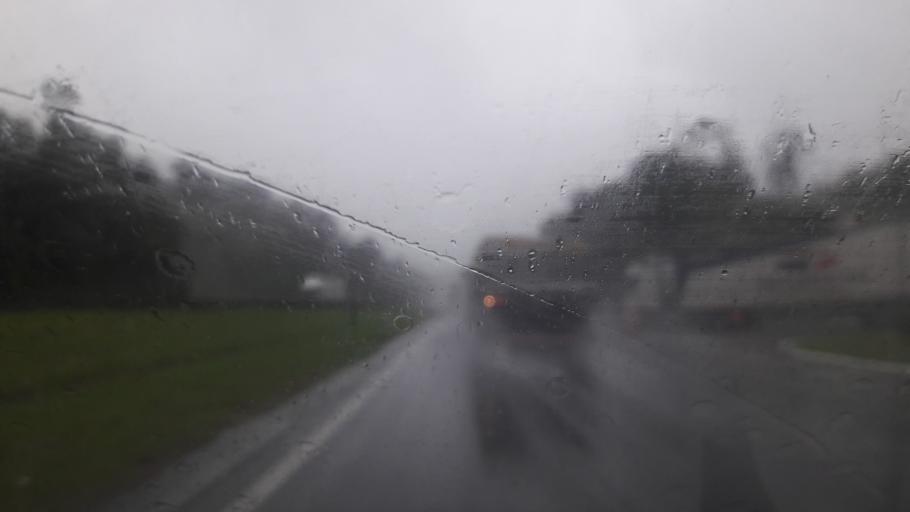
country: BR
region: Parana
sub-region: Antonina
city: Antonina
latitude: -25.1026
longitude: -48.7214
